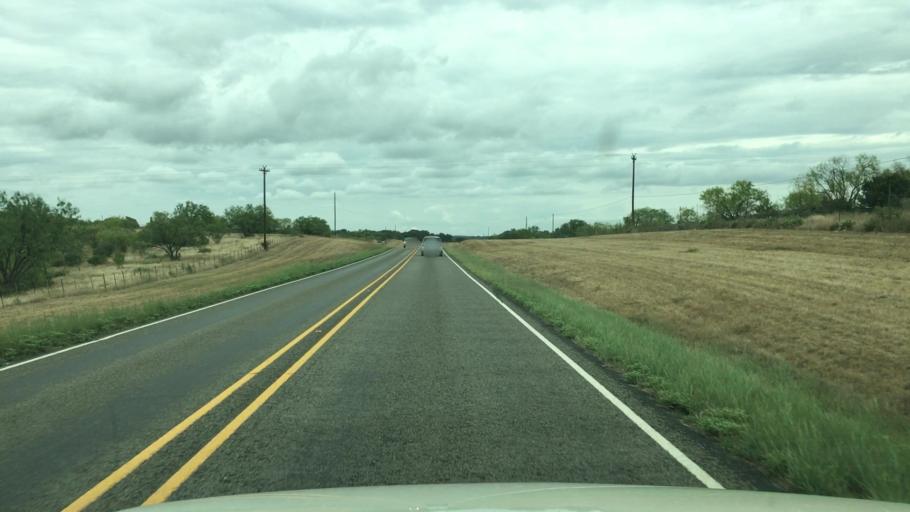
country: US
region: Texas
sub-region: Llano County
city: Kingsland
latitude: 30.5774
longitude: -98.4937
